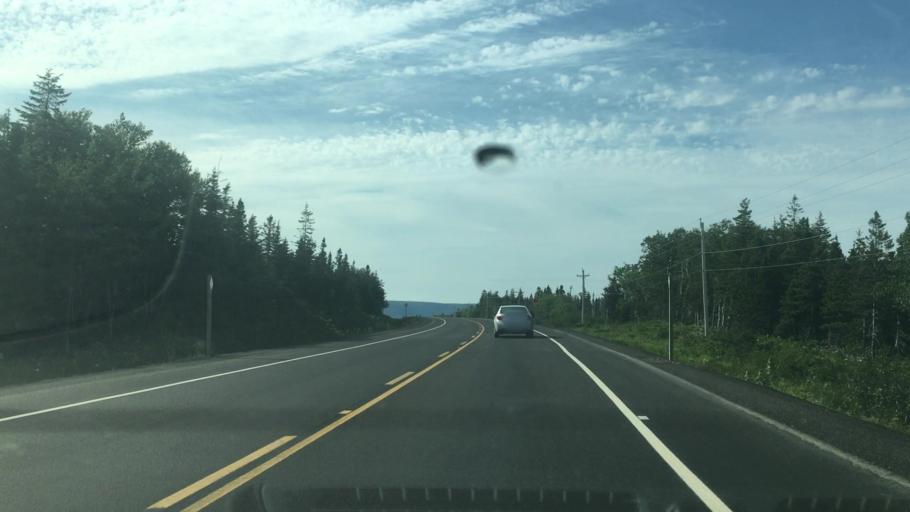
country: CA
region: Nova Scotia
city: Sydney Mines
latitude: 46.8483
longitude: -60.4158
